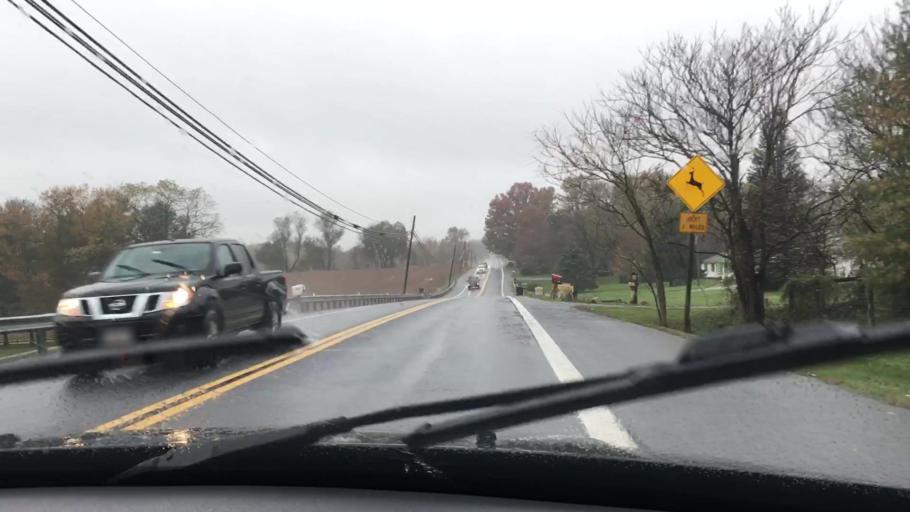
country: US
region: Maryland
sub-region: Frederick County
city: Urbana
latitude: 39.3231
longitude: -77.3638
